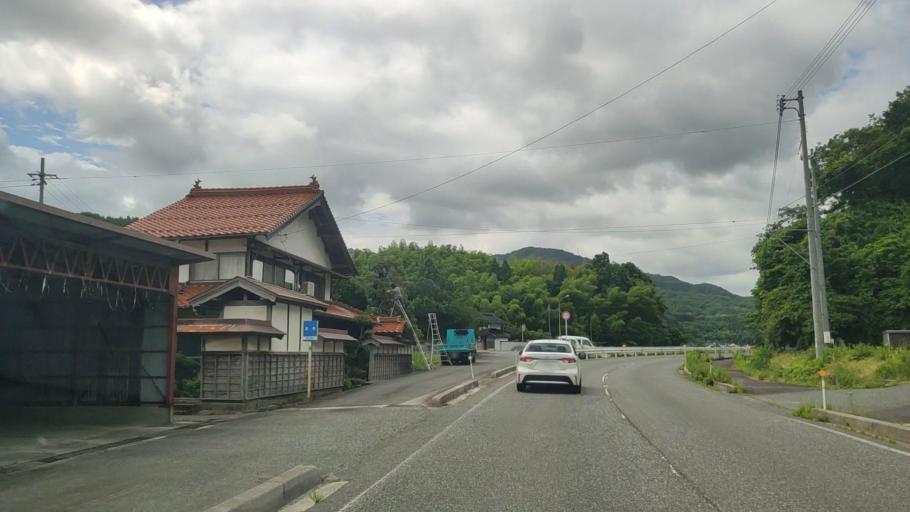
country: JP
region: Tottori
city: Yonago
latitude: 35.3277
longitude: 133.4336
